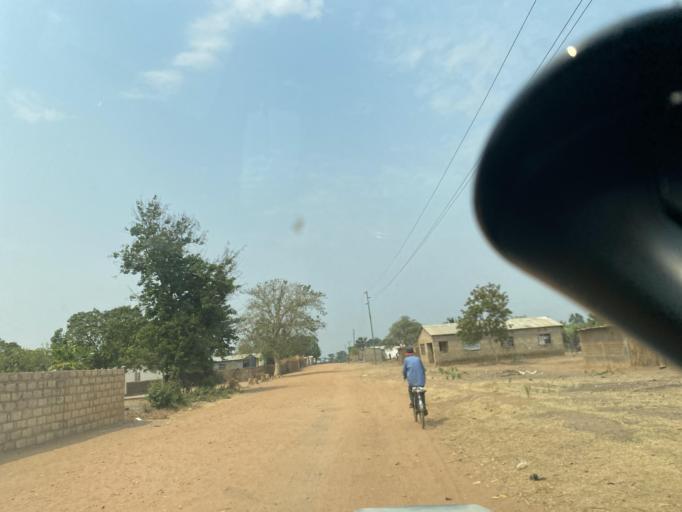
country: ZM
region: Lusaka
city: Kafue
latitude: -15.6685
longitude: 28.0187
